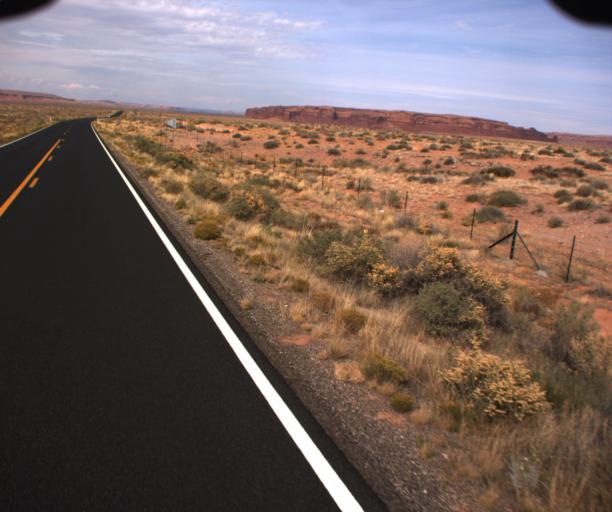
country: US
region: Arizona
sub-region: Apache County
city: Many Farms
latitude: 36.5615
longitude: -109.5405
